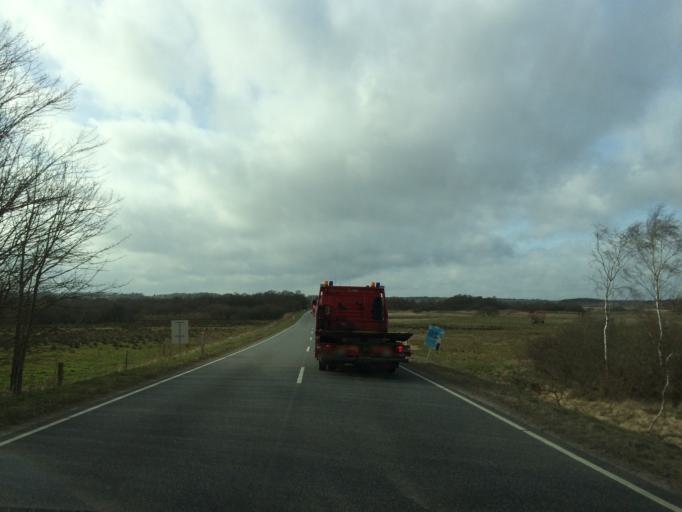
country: DK
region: Central Jutland
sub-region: Randers Kommune
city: Langa
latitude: 56.4871
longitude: 9.8648
